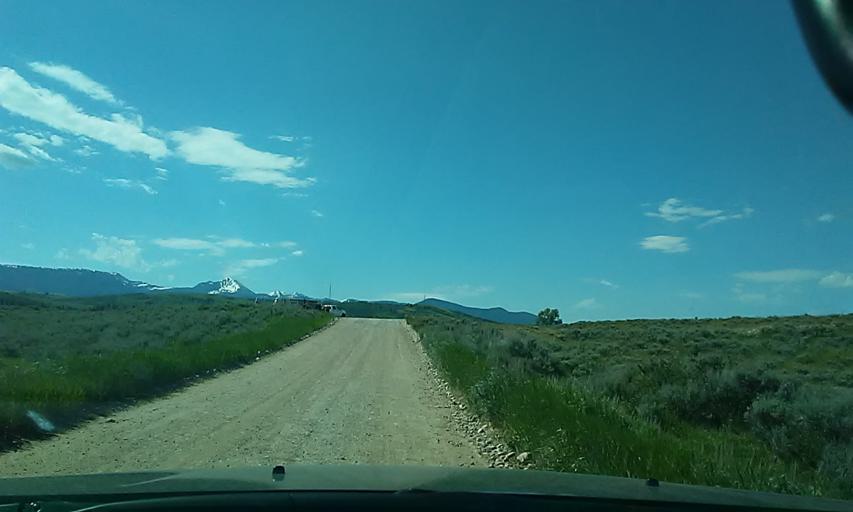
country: US
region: Wyoming
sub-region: Teton County
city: Jackson
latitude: 43.6271
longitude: -110.6642
